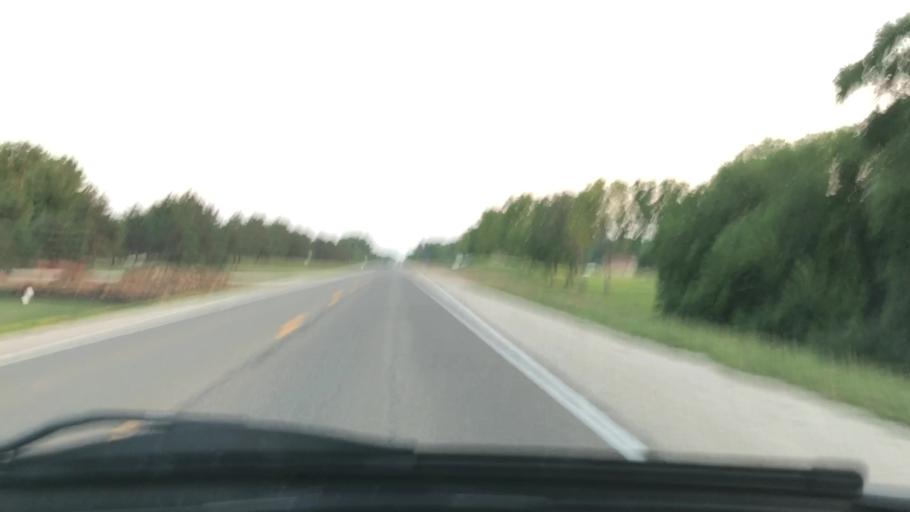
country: US
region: Iowa
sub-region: Henry County
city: Mount Pleasant
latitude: 40.9591
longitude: -91.5394
